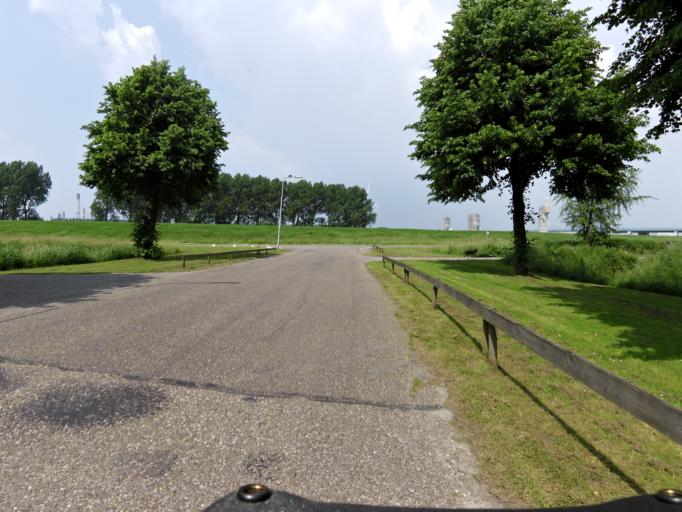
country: NL
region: South Holland
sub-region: Gemeente Spijkenisse
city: Spijkenisse
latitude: 51.8624
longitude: 4.3025
